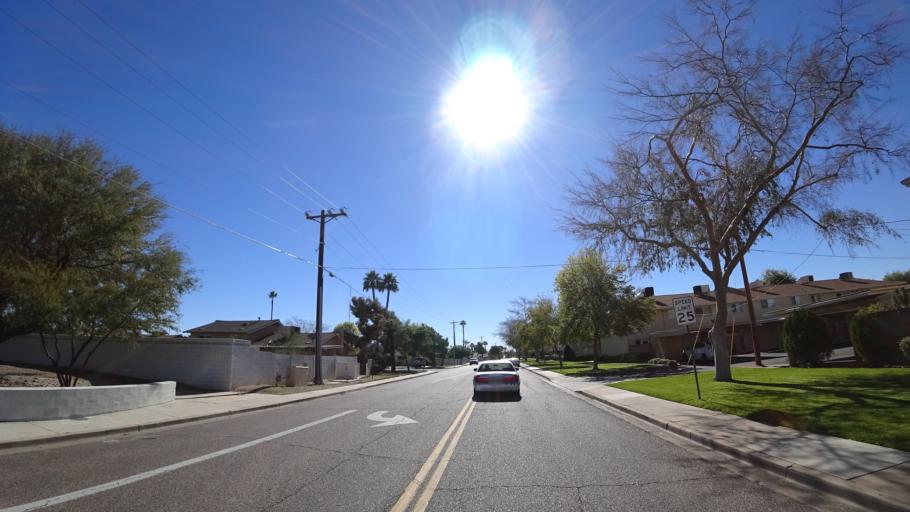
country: US
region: Arizona
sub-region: Maricopa County
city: Scottsdale
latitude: 33.5237
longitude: -111.8963
